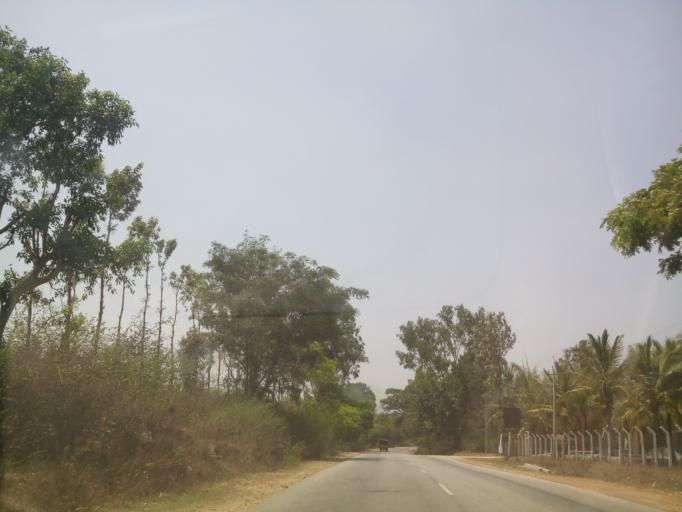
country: IN
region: Karnataka
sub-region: Hassan
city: Alur
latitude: 12.9542
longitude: 75.9769
